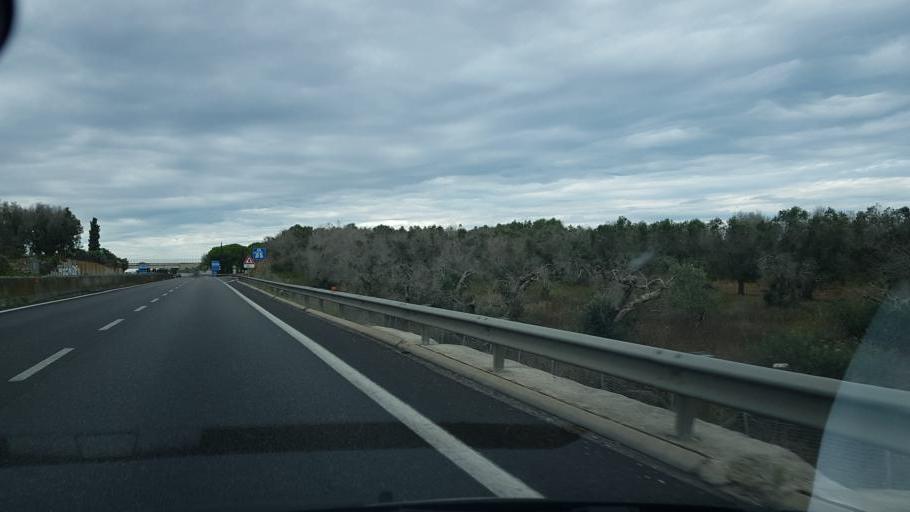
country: IT
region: Apulia
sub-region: Provincia di Brindisi
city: Torchiarolo
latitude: 40.4595
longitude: 18.0609
